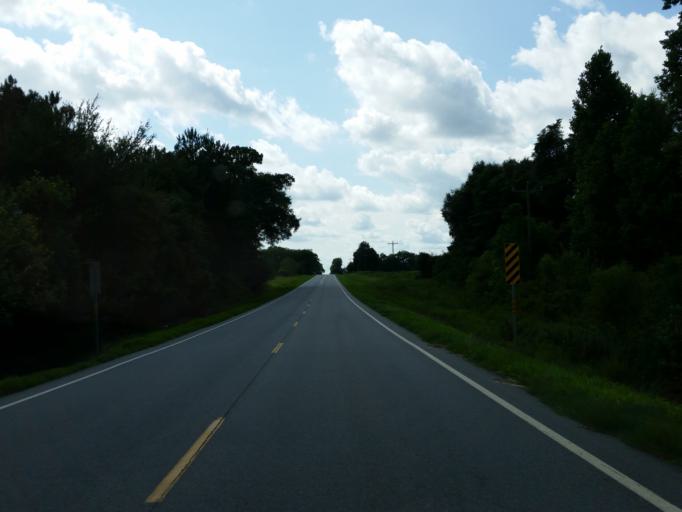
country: US
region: Georgia
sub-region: Turner County
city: Ashburn
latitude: 31.6493
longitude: -83.5437
